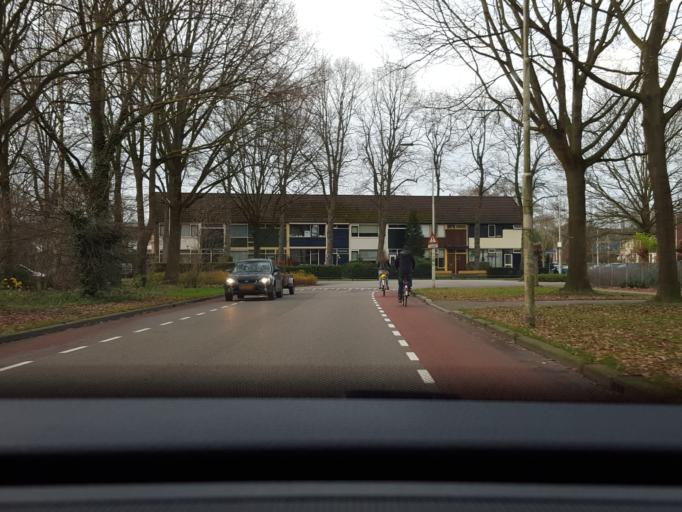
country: NL
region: Gelderland
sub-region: Gemeente Doetinchem
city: Doetinchem
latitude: 51.9741
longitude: 6.3022
